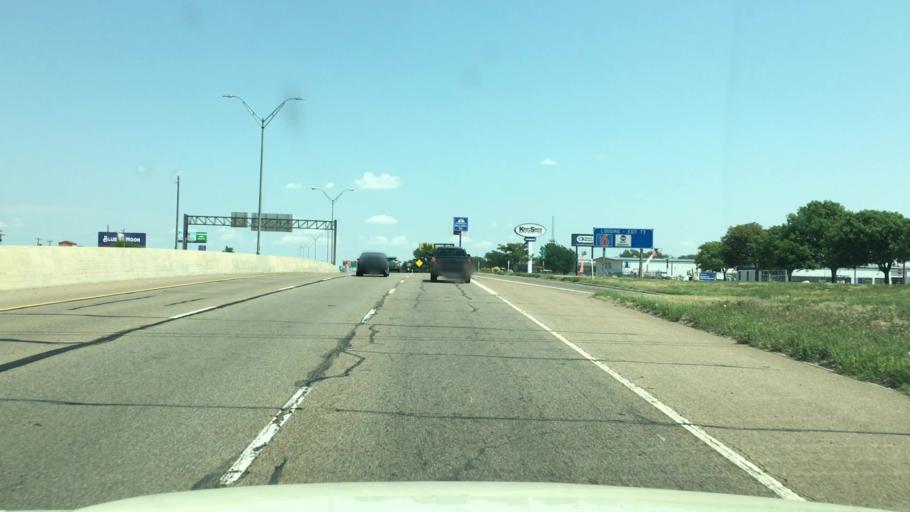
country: US
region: Texas
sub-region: Potter County
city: Amarillo
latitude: 35.1926
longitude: -101.7929
